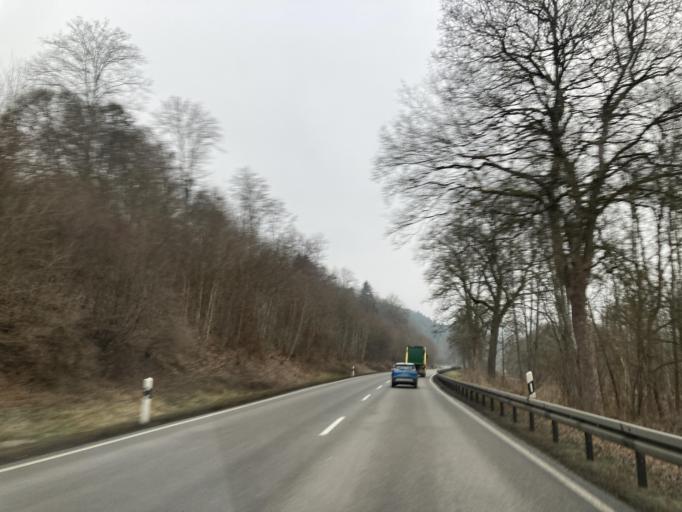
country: DE
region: Baden-Wuerttemberg
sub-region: Freiburg Region
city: Immendingen
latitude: 47.9426
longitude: 8.7594
